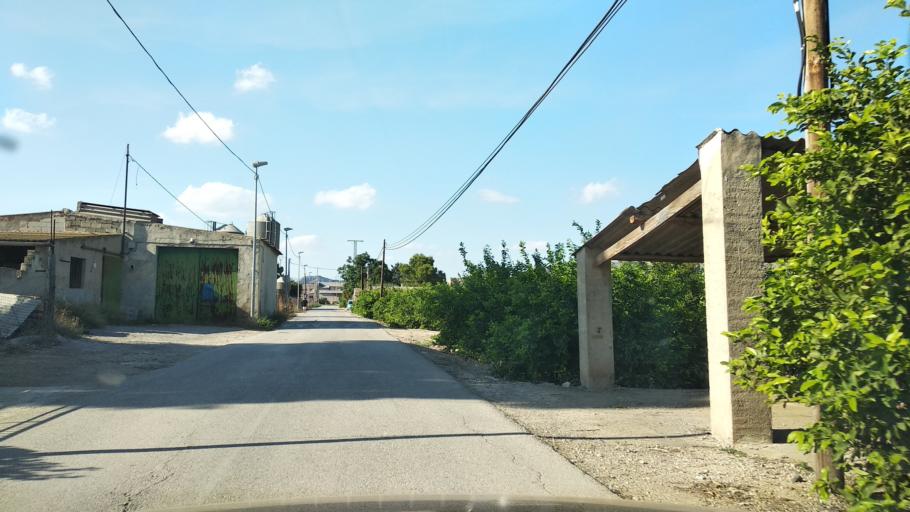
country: ES
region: Murcia
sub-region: Murcia
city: Santomera
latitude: 38.0535
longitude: -1.0418
